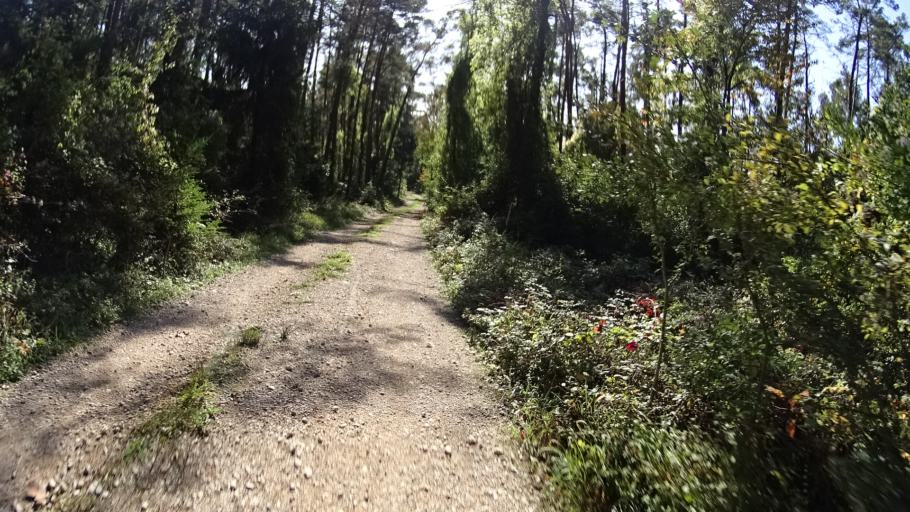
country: DE
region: Bavaria
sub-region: Upper Bavaria
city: Hitzhofen
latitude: 48.8443
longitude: 11.3463
